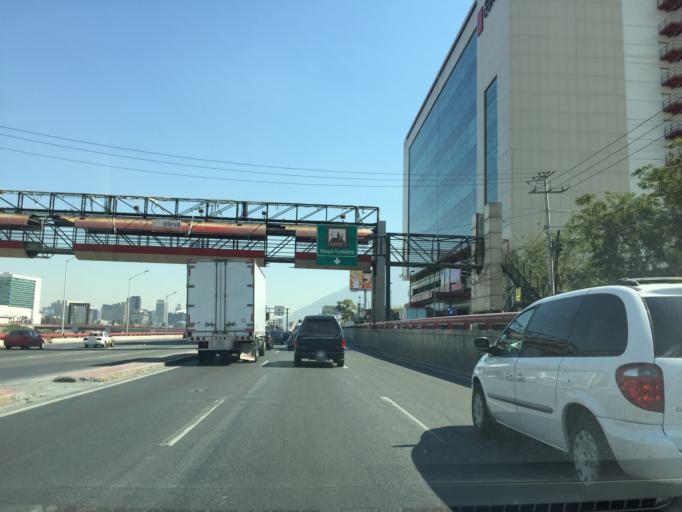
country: MX
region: Nuevo Leon
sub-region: Monterrey
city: Monterrey
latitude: 25.6653
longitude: -100.3314
